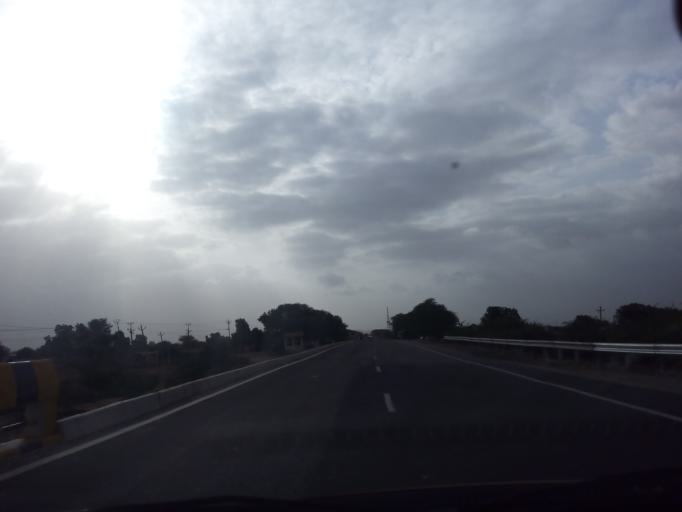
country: IN
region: Gujarat
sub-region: Kachchh
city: Anjar
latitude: 23.2945
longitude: 70.0753
